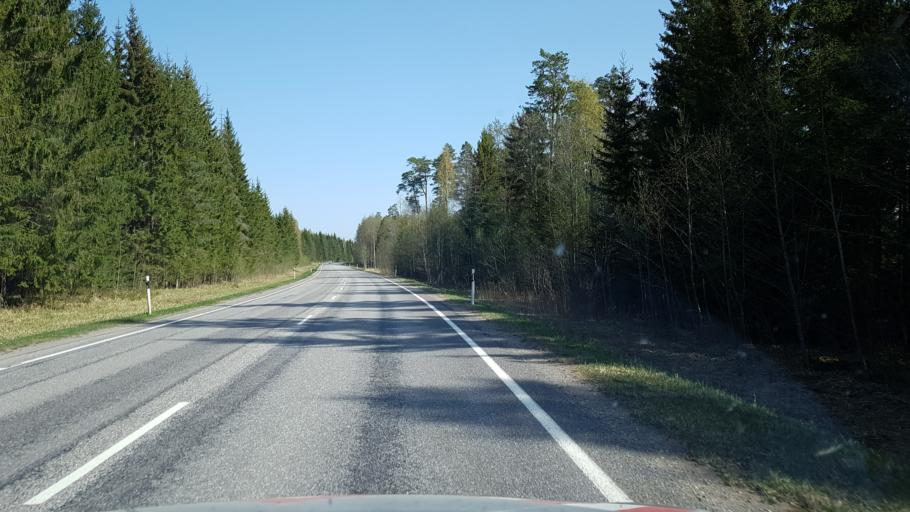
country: EE
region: Viljandimaa
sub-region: Moisakuela linn
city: Moisakula
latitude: 58.2316
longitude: 25.1166
